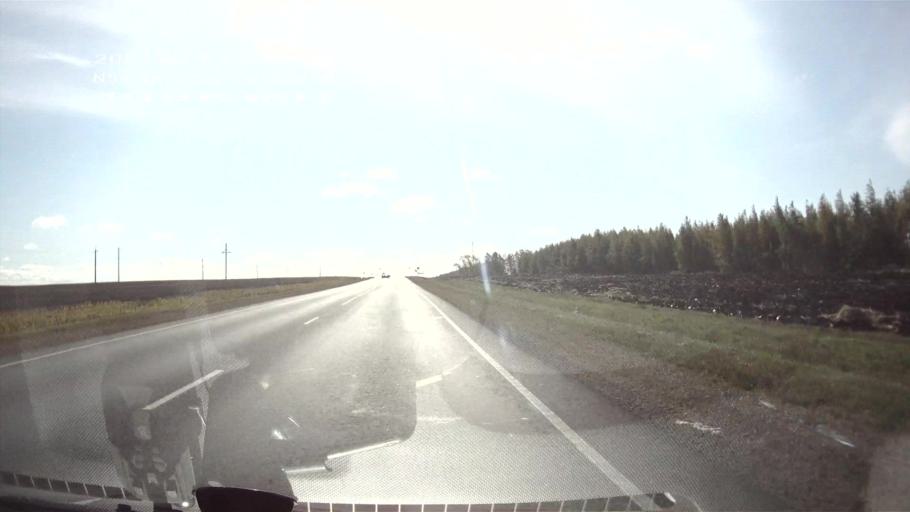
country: RU
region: Ulyanovsk
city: Tsil'na
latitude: 54.5820
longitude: 47.8901
